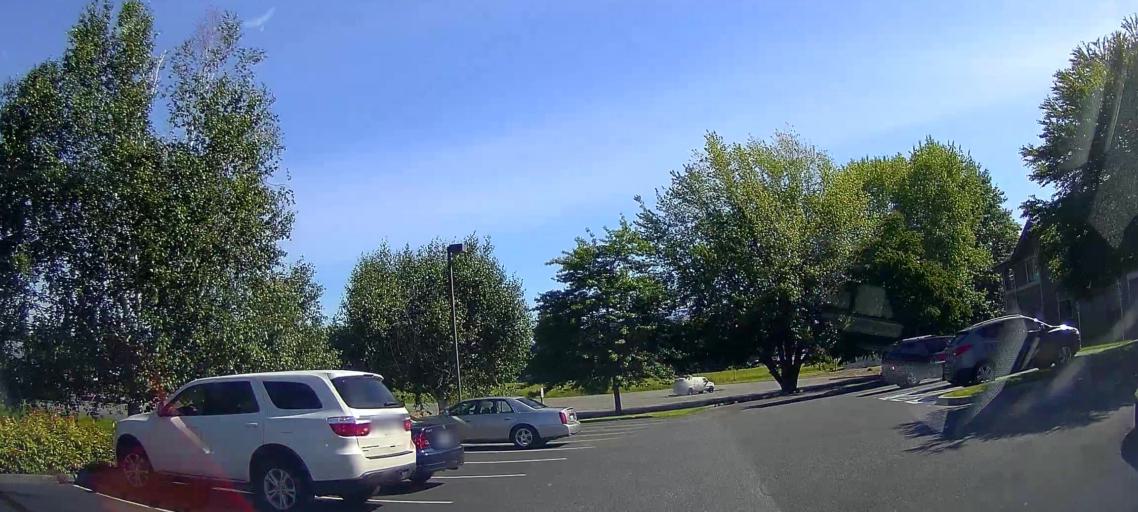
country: US
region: Washington
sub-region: Skagit County
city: Sedro-Woolley
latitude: 48.4963
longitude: -122.2800
